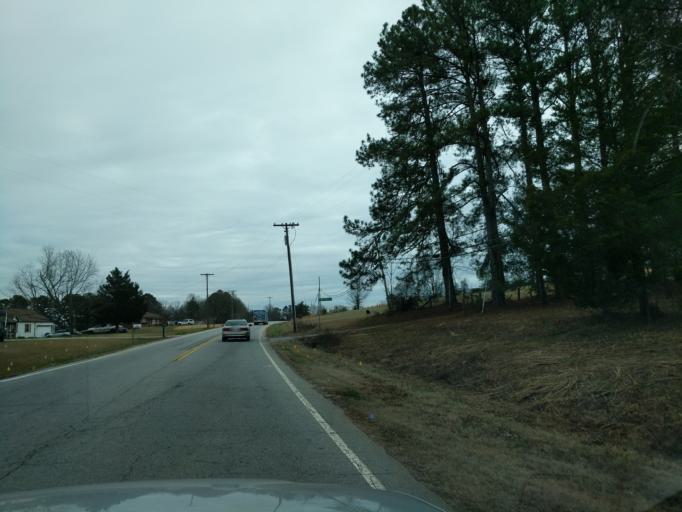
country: US
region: South Carolina
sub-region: Oconee County
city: Westminster
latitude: 34.6806
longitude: -83.1195
